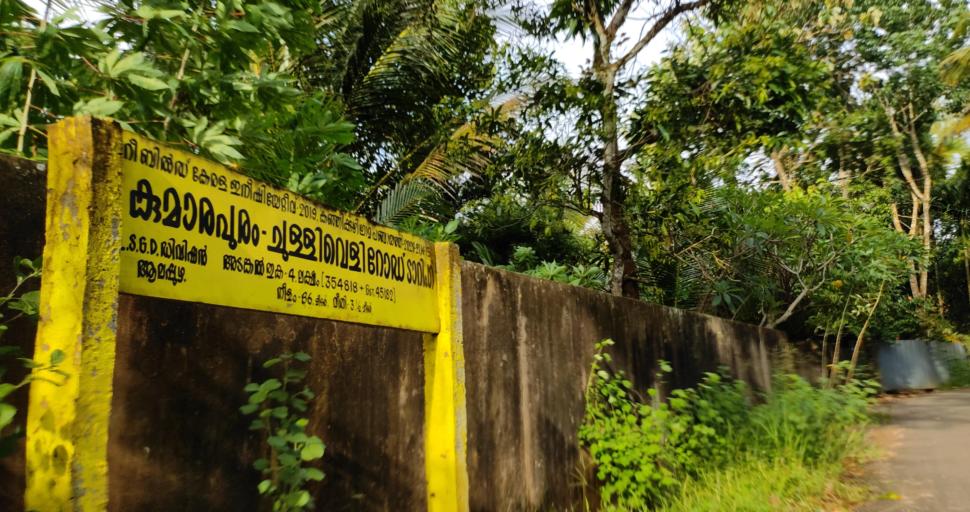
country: IN
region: Kerala
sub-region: Alappuzha
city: Shertallai
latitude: 9.6144
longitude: 76.3463
